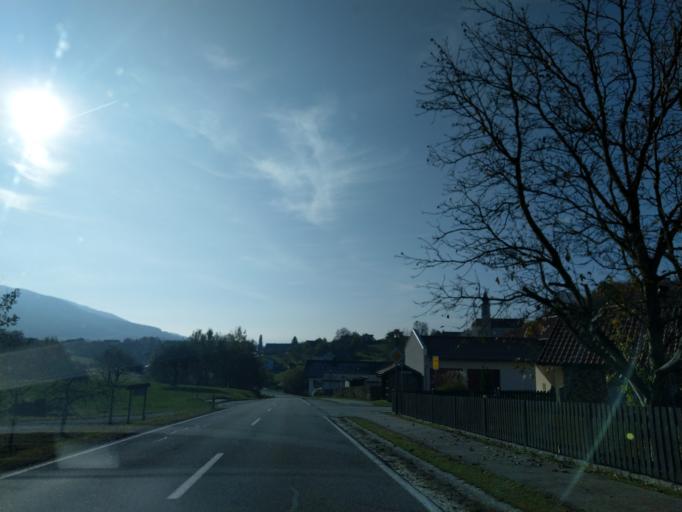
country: DE
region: Bavaria
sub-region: Lower Bavaria
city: Lalling
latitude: 48.8500
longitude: 13.1388
